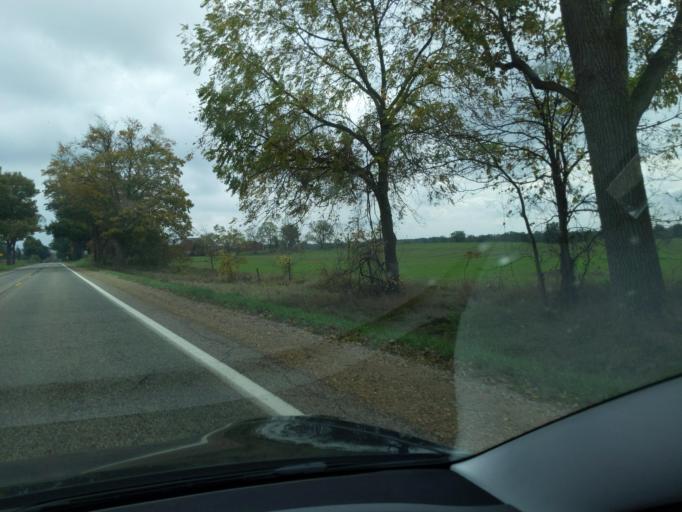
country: US
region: Michigan
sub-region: Eaton County
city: Potterville
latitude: 42.5473
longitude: -84.7477
